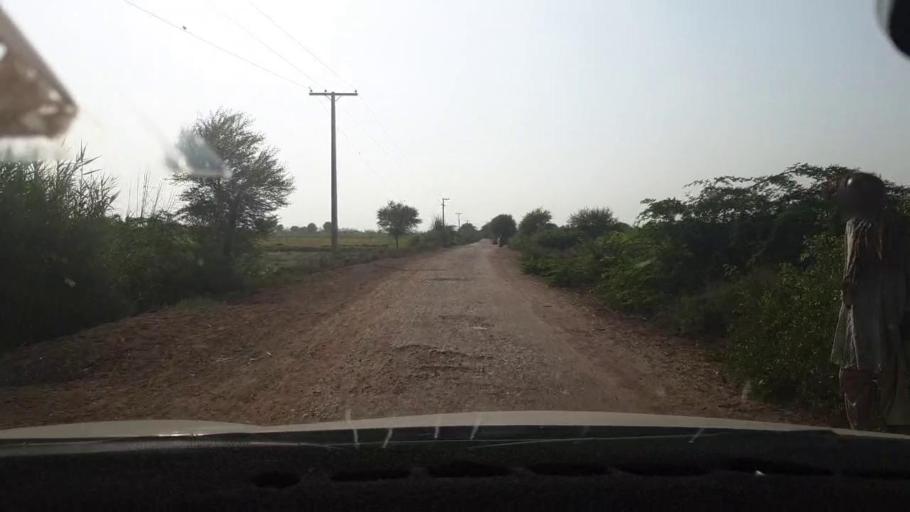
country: PK
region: Sindh
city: Berani
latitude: 25.7502
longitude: 68.8001
